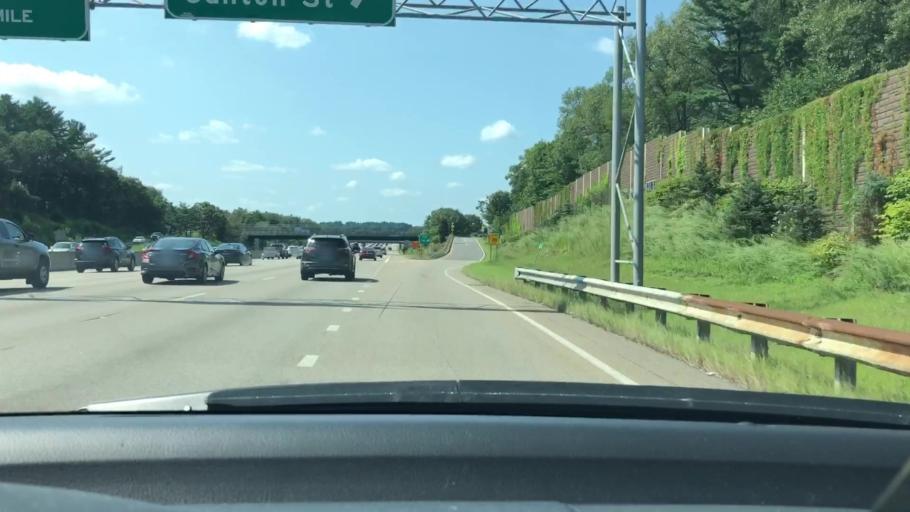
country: US
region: Massachusetts
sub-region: Norfolk County
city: Dedham
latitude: 42.2217
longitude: -71.1663
